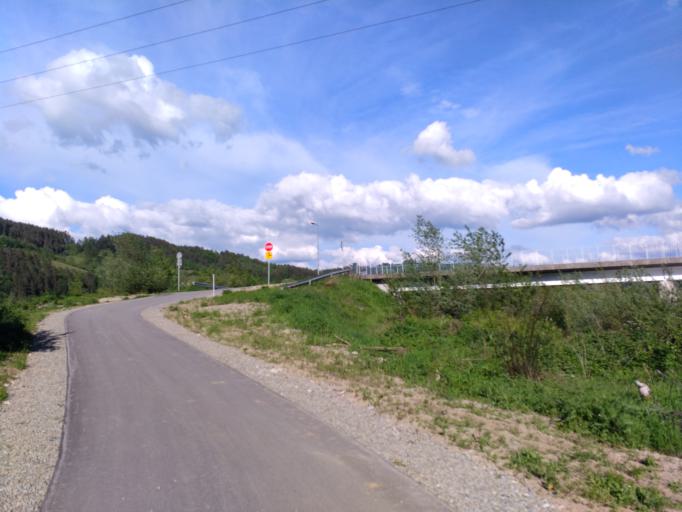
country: PL
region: Lesser Poland Voivodeship
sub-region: Powiat nowosadecki
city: Lacko
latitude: 49.5396
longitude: 20.4727
